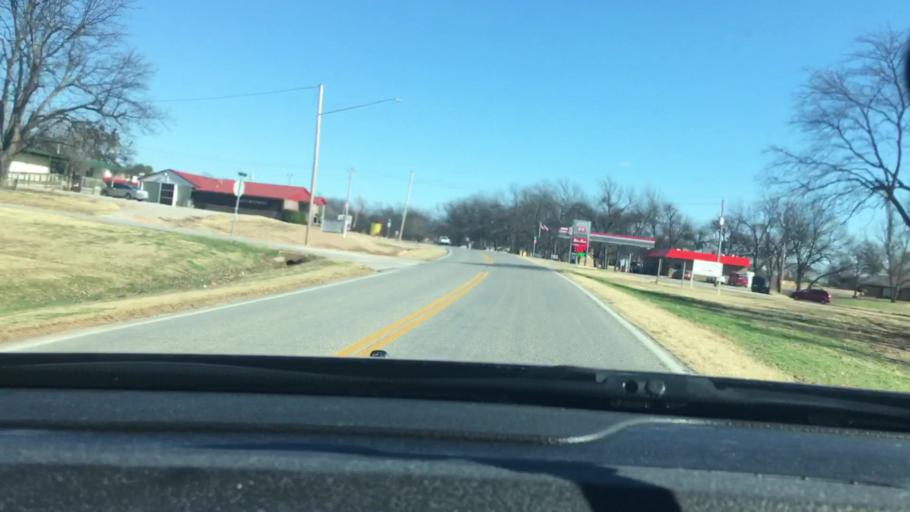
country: US
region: Oklahoma
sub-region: Garvin County
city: Wynnewood
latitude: 34.6446
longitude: -97.1571
